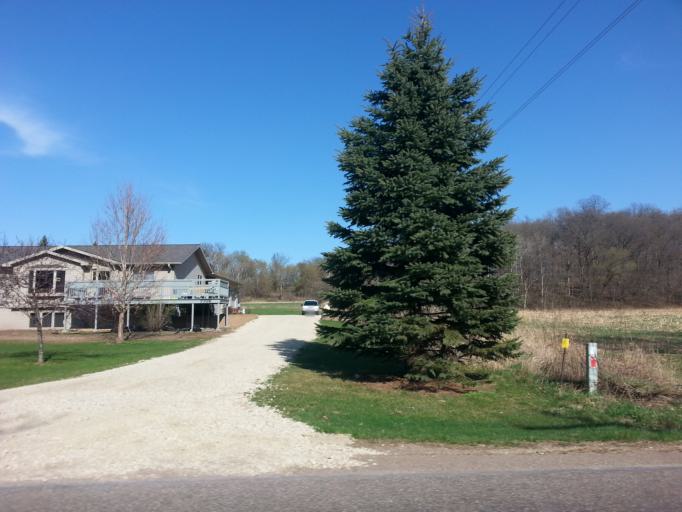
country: US
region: Wisconsin
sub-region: Pierce County
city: River Falls
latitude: 44.8195
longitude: -92.5782
